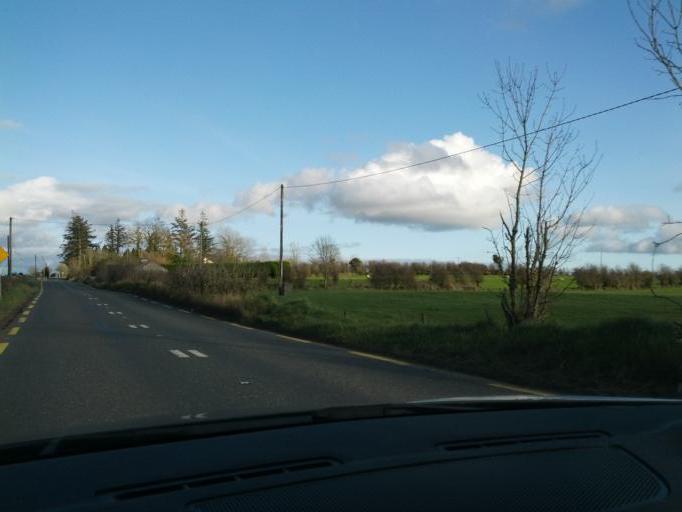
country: IE
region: Connaught
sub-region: Roscommon
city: Roscommon
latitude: 53.6520
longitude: -8.2468
